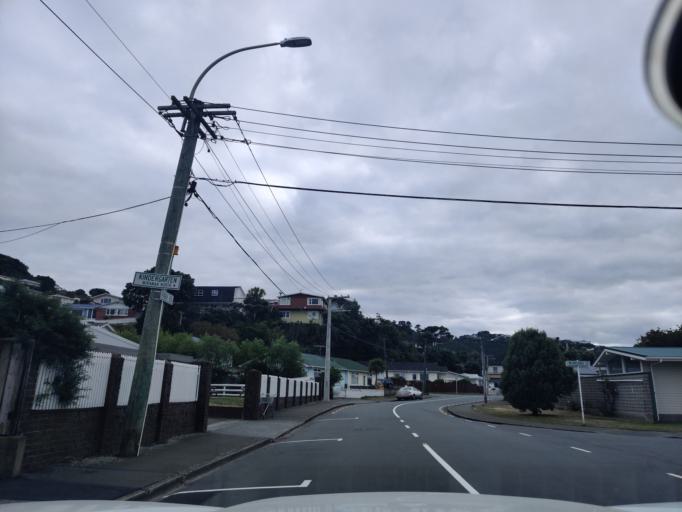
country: NZ
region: Wellington
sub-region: Wellington City
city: Wellington
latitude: -41.3075
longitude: 174.8220
